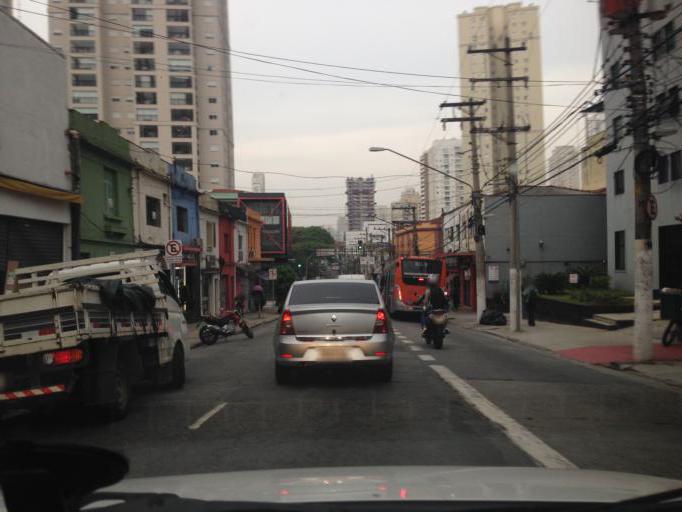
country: BR
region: Sao Paulo
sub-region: Sao Paulo
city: Sao Paulo
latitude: -23.5246
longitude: -46.7039
